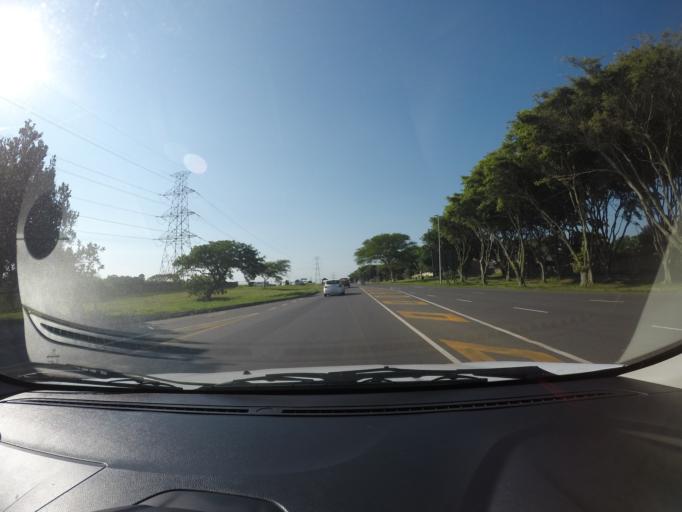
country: ZA
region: KwaZulu-Natal
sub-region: uThungulu District Municipality
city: Richards Bay
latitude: -28.7307
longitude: 32.0383
